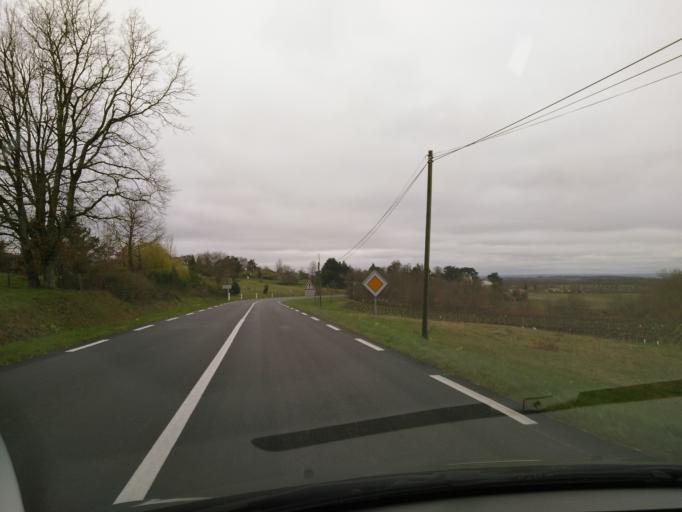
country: FR
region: Aquitaine
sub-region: Departement de la Dordogne
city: Monbazillac
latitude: 44.7366
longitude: 0.5429
